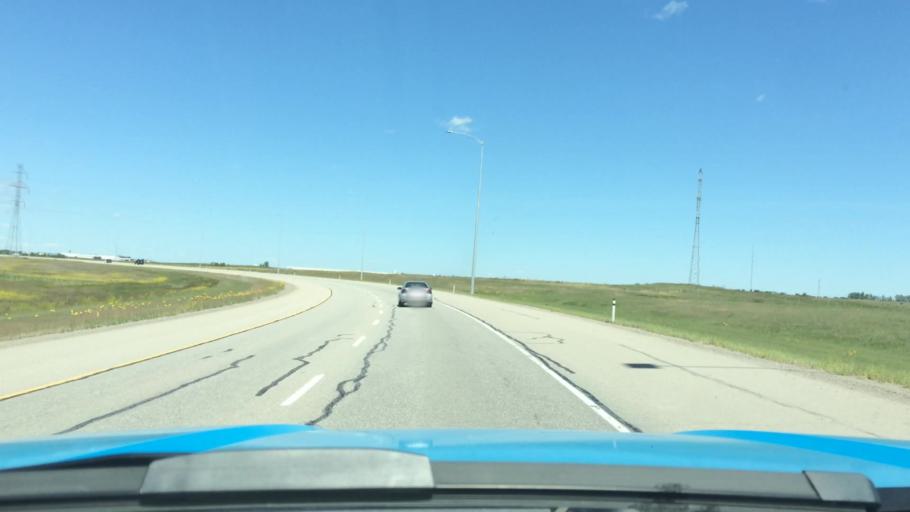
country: CA
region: Alberta
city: Chestermere
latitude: 51.1741
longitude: -113.9135
